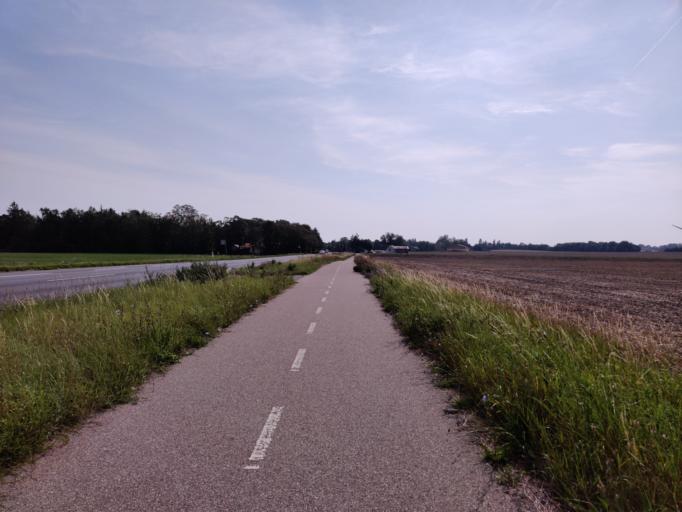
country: DK
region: Zealand
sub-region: Guldborgsund Kommune
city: Nykobing Falster
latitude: 54.6858
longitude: 11.9052
